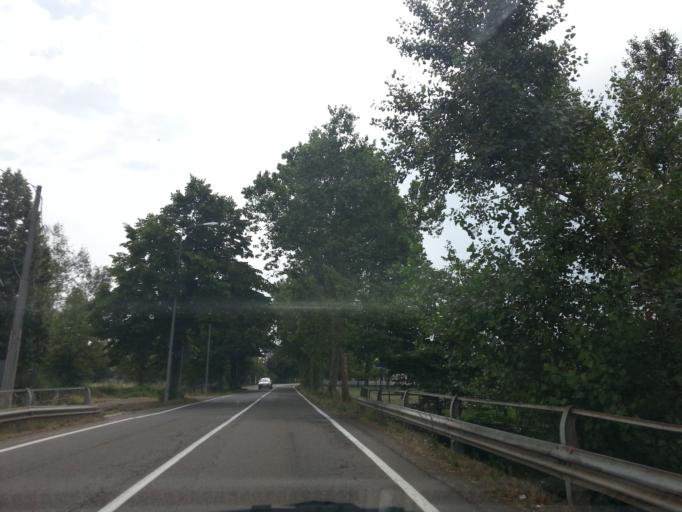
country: IT
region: Emilia-Romagna
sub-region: Provincia di Reggio Emilia
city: Albinea
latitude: 44.6554
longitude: 10.5991
